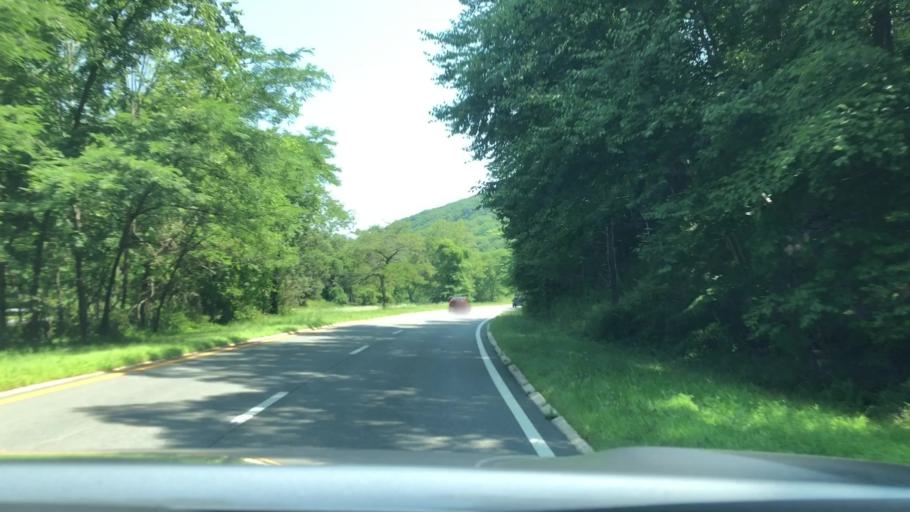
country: US
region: New York
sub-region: Orange County
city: Fort Montgomery
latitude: 41.3114
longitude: -74.0221
